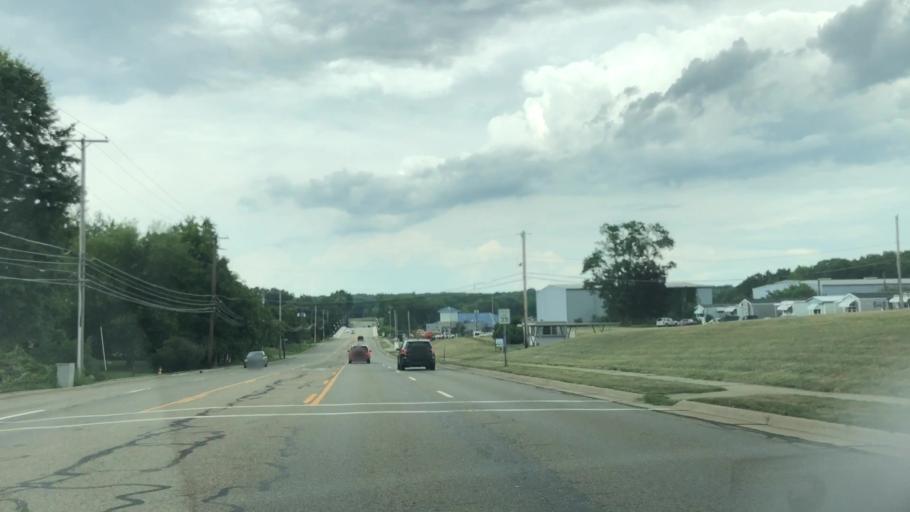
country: US
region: Ohio
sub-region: Summit County
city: Portage Lakes
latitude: 40.9832
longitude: -81.5220
